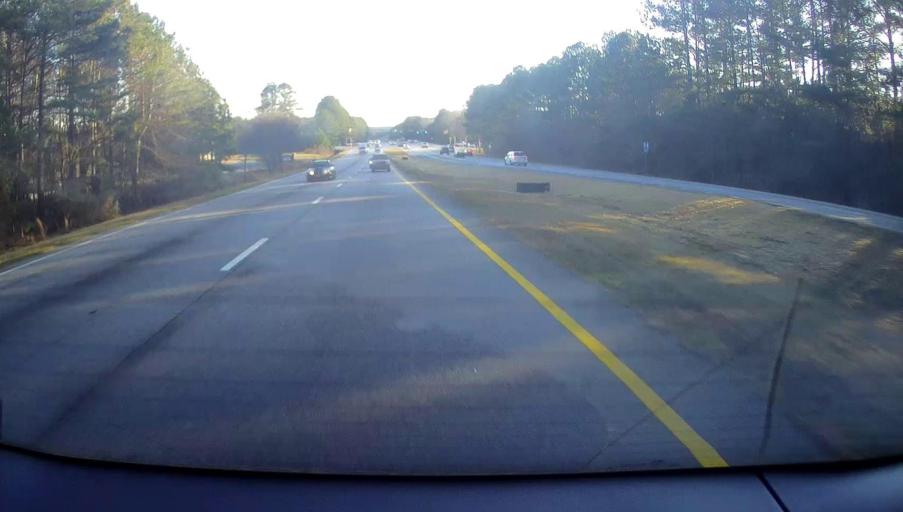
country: US
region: Georgia
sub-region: Fayette County
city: Tyrone
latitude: 33.4809
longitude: -84.5856
